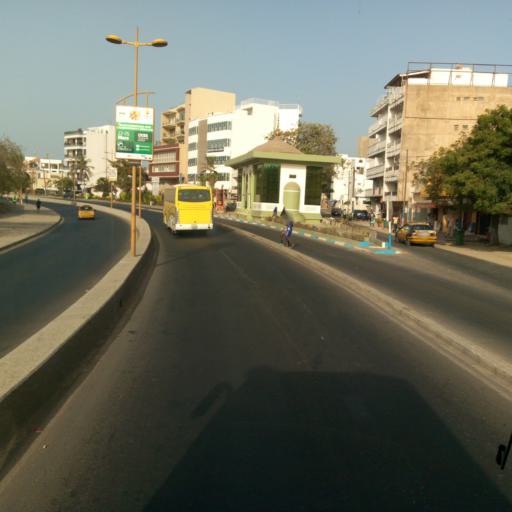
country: SN
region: Dakar
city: Dakar
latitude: 14.6776
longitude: -17.4582
